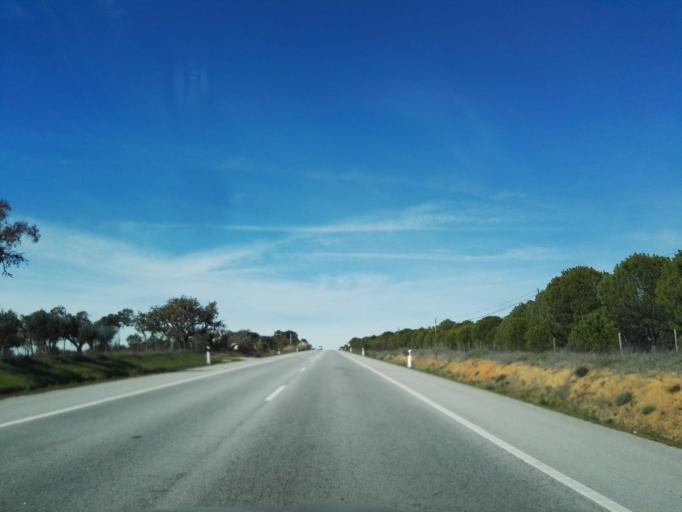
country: PT
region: Portalegre
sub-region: Arronches
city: Arronches
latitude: 39.1459
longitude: -7.3047
